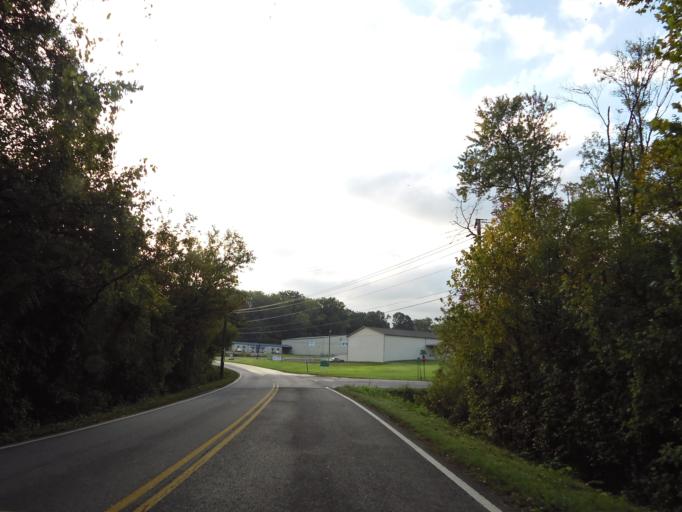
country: US
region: Tennessee
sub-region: Blount County
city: Eagleton Village
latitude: 35.8301
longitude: -83.9521
